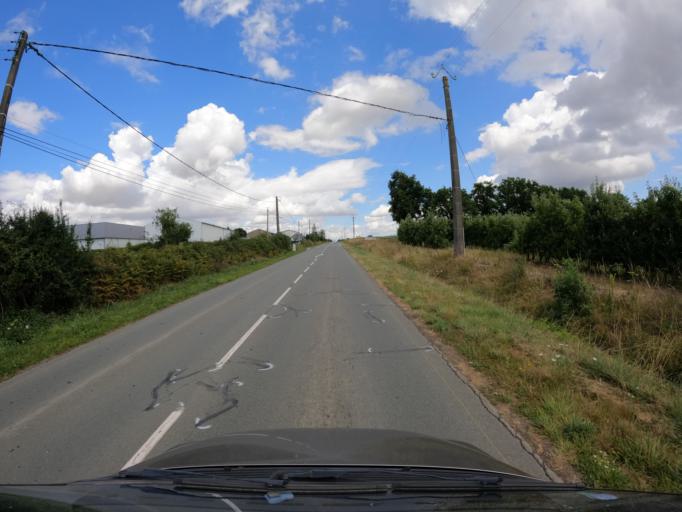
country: FR
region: Pays de la Loire
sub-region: Departement de Maine-et-Loire
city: Champigne
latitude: 47.6778
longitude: -0.5617
